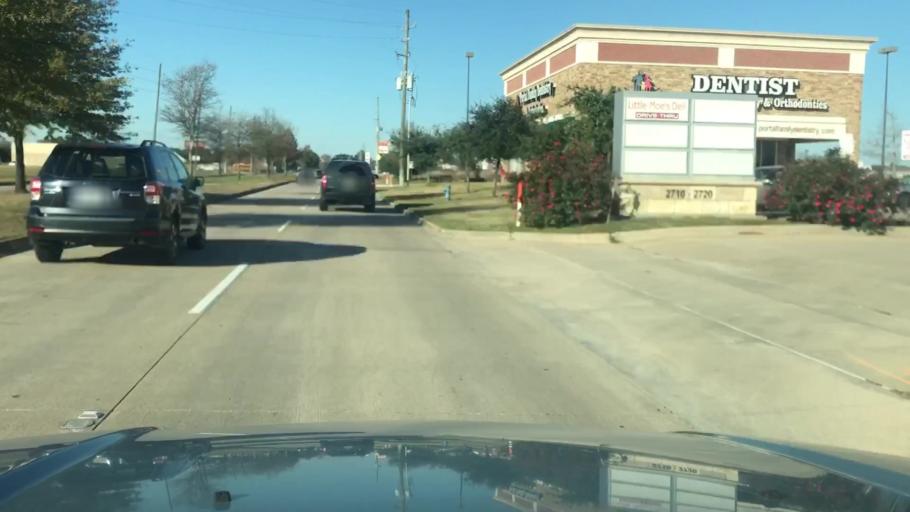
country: US
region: Texas
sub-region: Fort Bend County
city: Cinco Ranch
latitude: 29.8137
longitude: -95.7521
